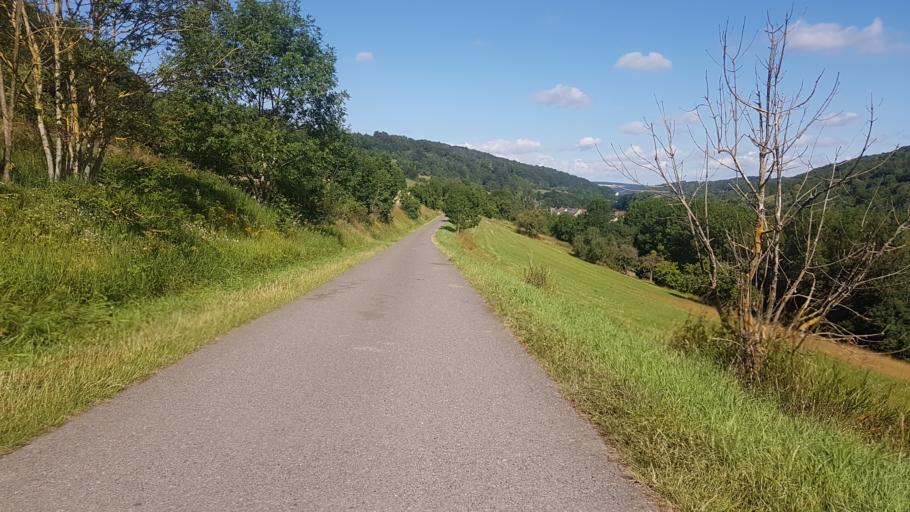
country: DE
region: Baden-Wuerttemberg
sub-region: Regierungsbezirk Stuttgart
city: Creglingen
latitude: 49.4506
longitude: 10.0753
